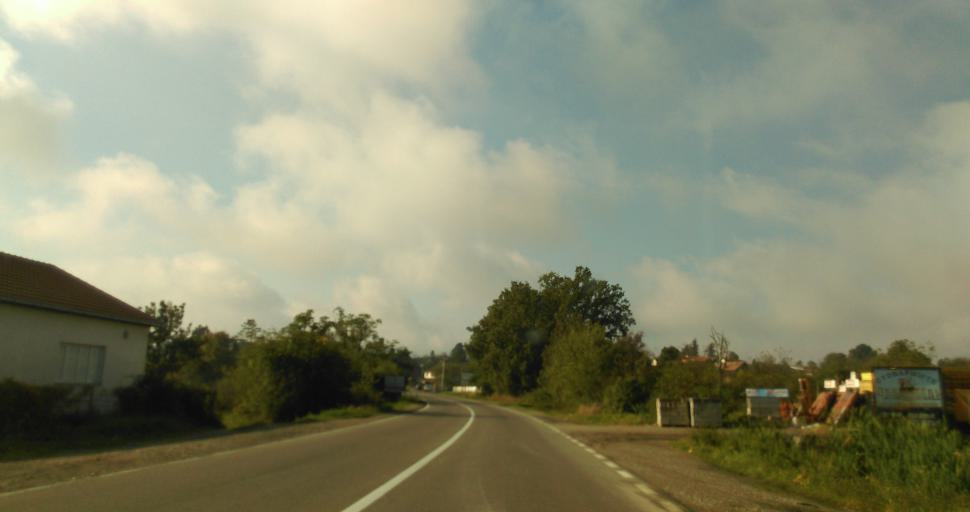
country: RS
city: Vranic
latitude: 44.6057
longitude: 20.3545
